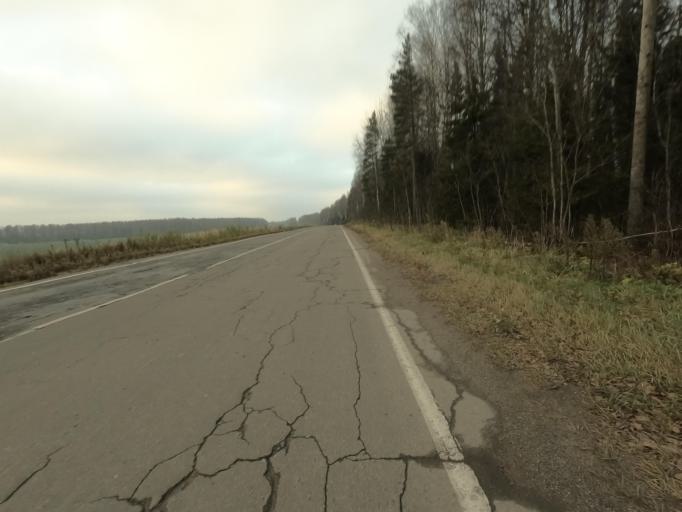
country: RU
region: Leningrad
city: Mga
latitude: 59.7955
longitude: 31.0046
